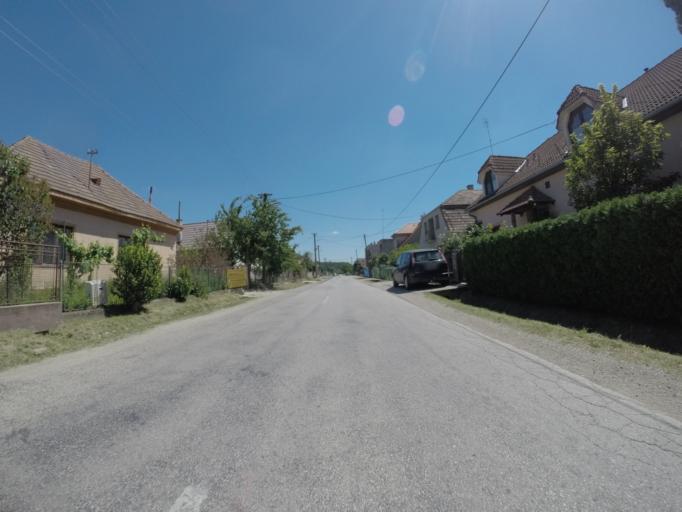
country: SK
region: Trnavsky
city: Hlohovec
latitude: 48.4883
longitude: 17.8828
